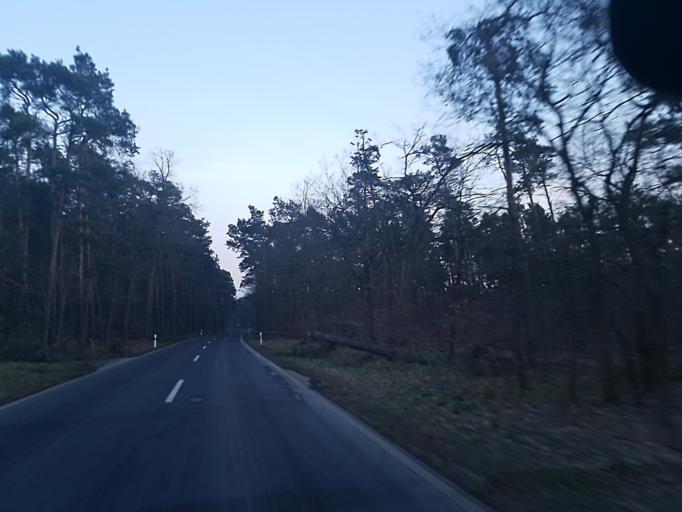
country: DE
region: Saxony-Anhalt
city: Holzdorf
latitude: 51.7785
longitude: 13.0754
